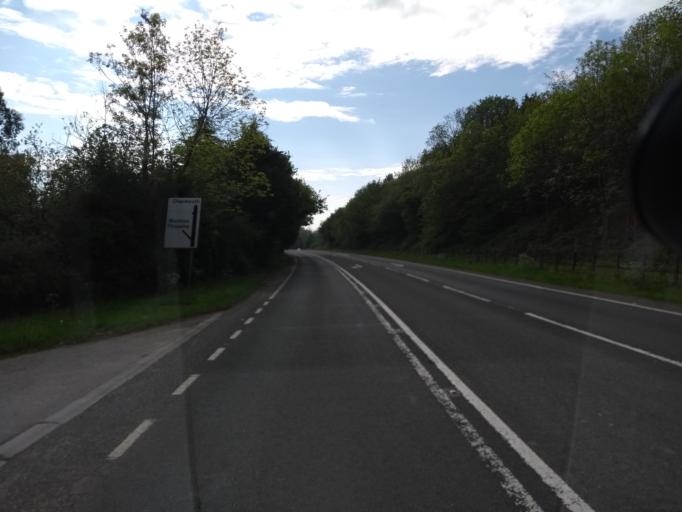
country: GB
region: England
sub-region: Dorset
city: Lyme Regis
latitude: 50.7510
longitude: -2.9297
